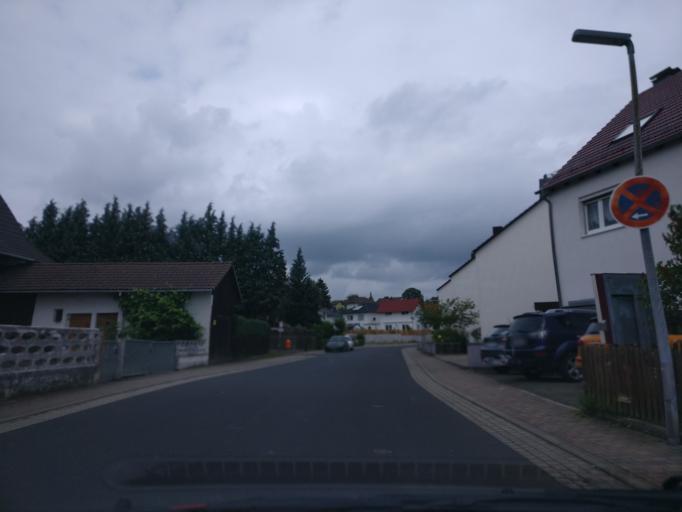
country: DE
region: Hesse
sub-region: Regierungsbezirk Kassel
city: Kassel
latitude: 51.3518
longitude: 9.5297
